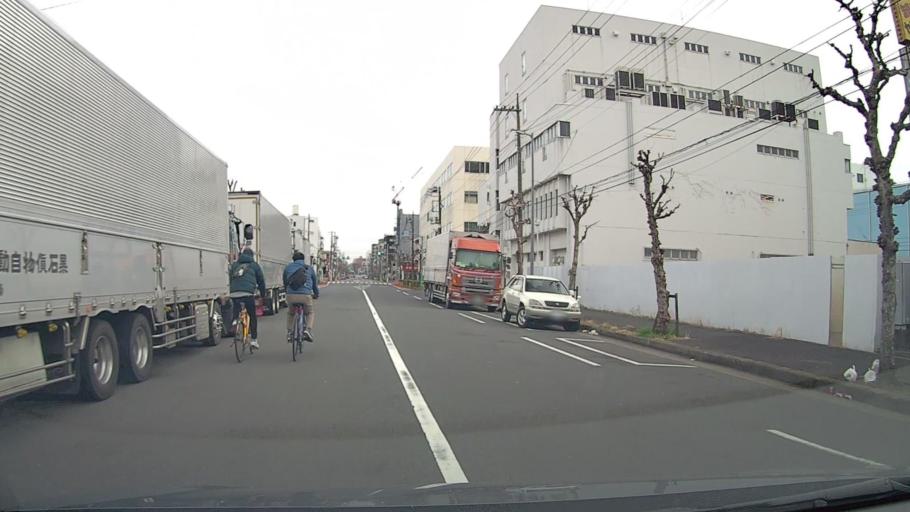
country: JP
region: Saitama
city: Wako
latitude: 35.7922
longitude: 139.6520
